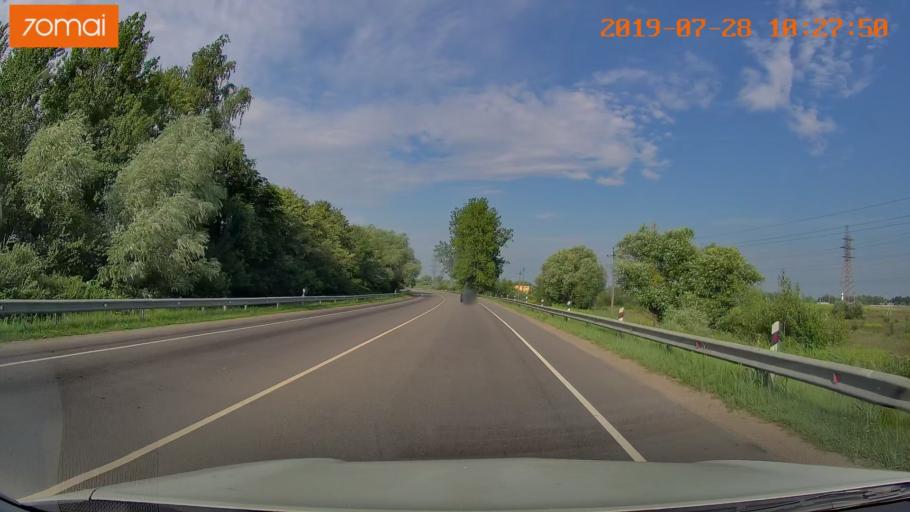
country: RU
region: Kaliningrad
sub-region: Gorod Kaliningrad
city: Kaliningrad
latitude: 54.7716
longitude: 20.5099
